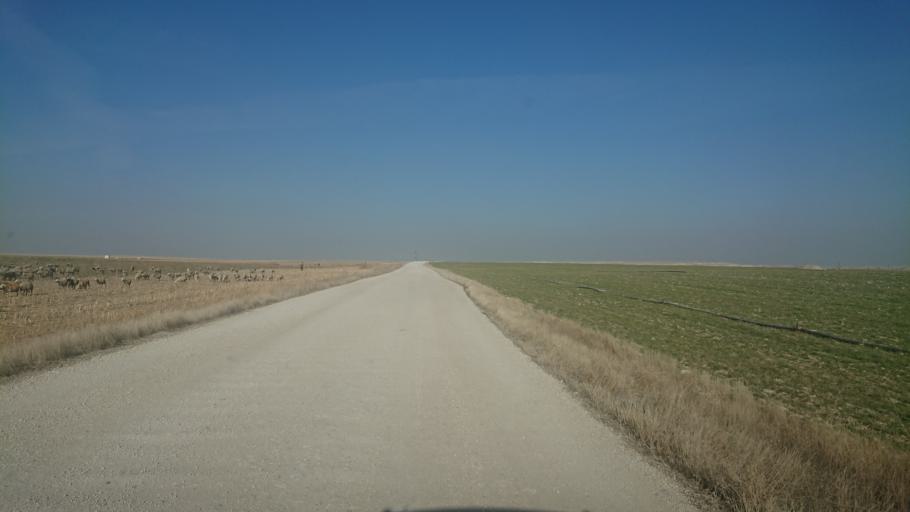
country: TR
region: Aksaray
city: Sultanhani
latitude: 38.0443
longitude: 33.6066
